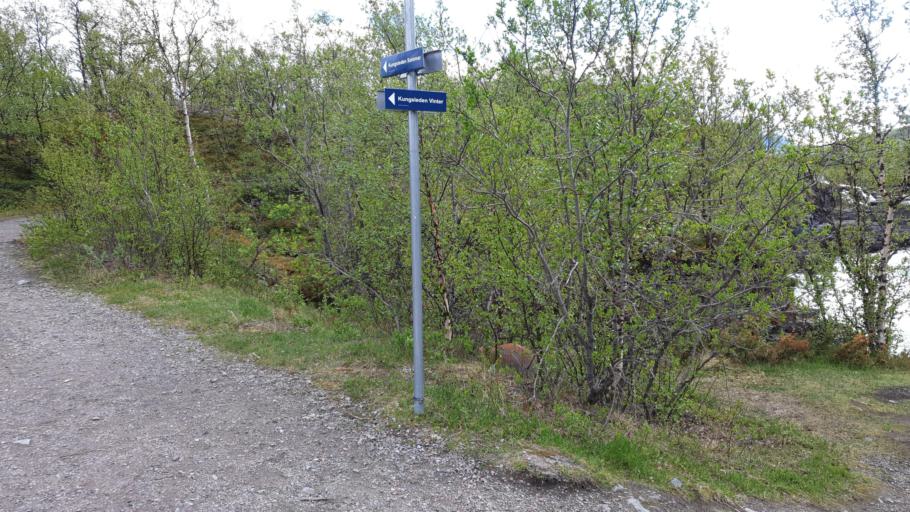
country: NO
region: Troms
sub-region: Bardu
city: Setermoen
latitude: 68.3586
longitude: 18.7754
